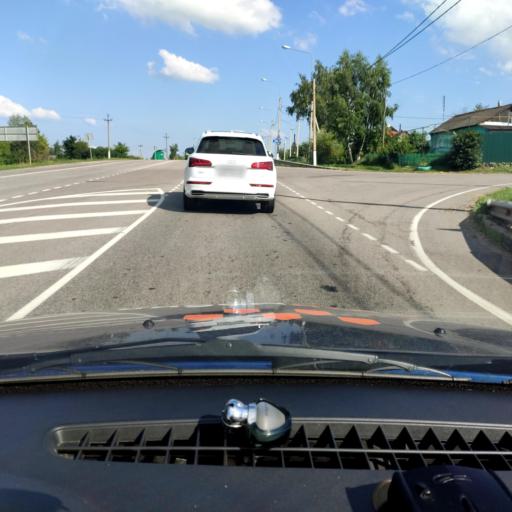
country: RU
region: Lipetsk
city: Yelets
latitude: 52.5558
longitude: 38.6994
